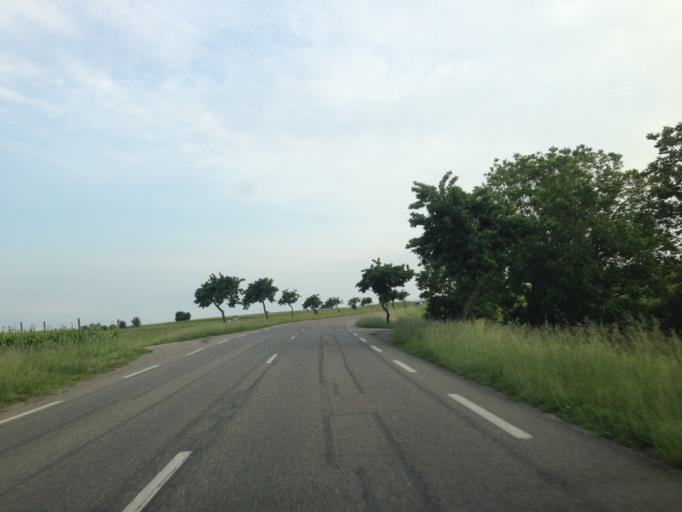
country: FR
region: Alsace
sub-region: Departement du Haut-Rhin
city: Ribeauville
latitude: 48.1794
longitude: 7.3241
